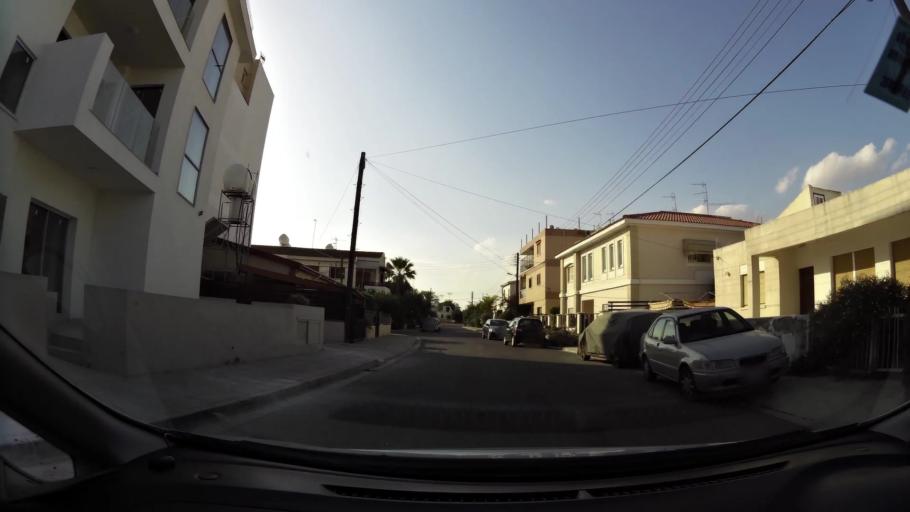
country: CY
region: Lefkosia
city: Nicosia
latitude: 35.1762
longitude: 33.3328
